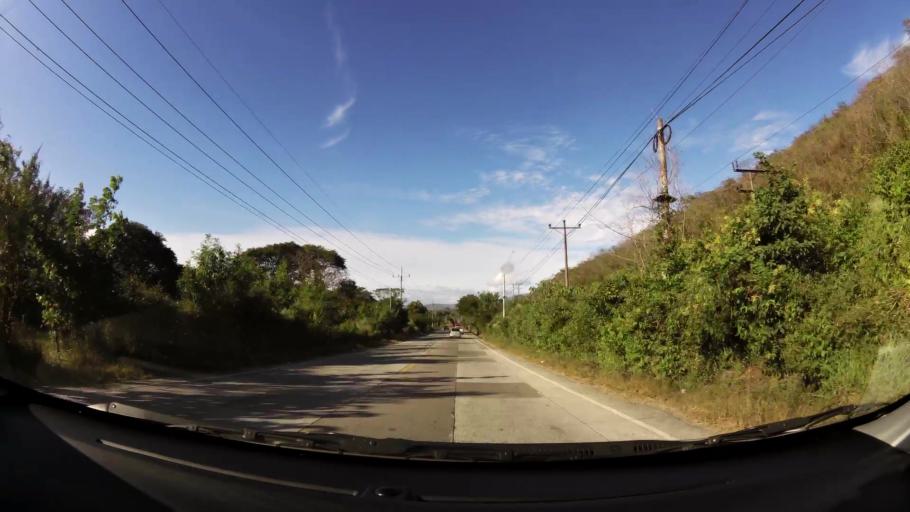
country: SV
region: Santa Ana
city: Metapan
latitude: 14.2711
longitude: -89.4605
